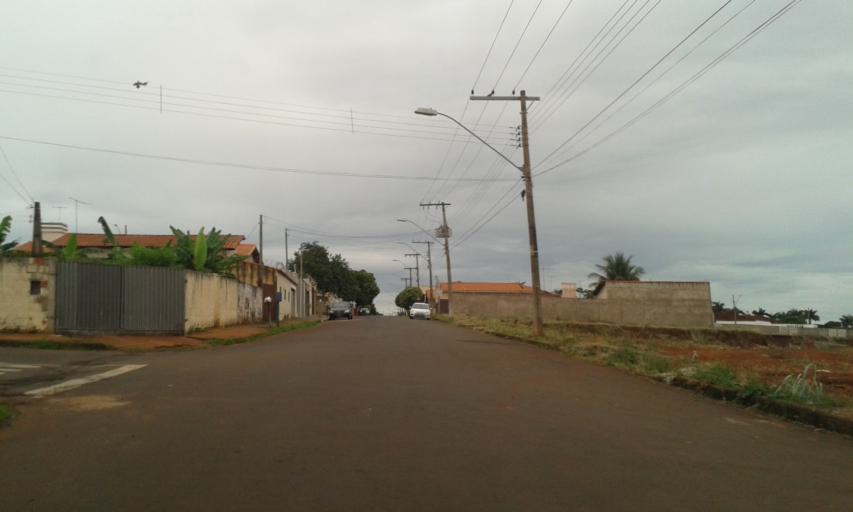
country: BR
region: Minas Gerais
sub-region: Ituiutaba
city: Ituiutaba
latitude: -18.9770
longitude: -49.4480
